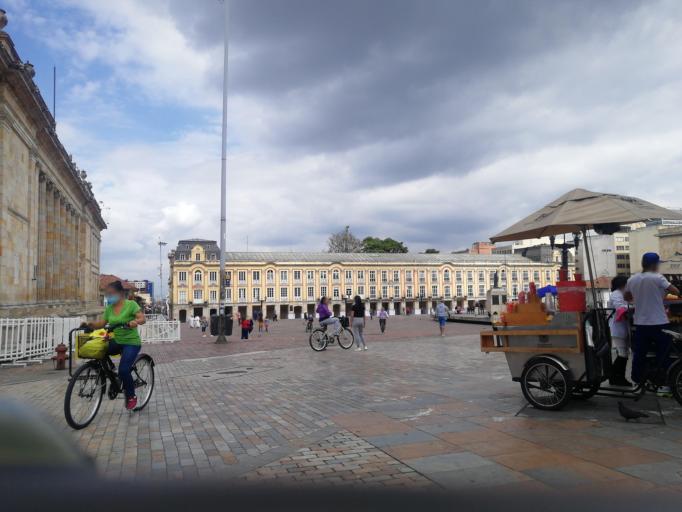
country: CO
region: Bogota D.C.
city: Bogota
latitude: 4.5972
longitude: -74.0759
